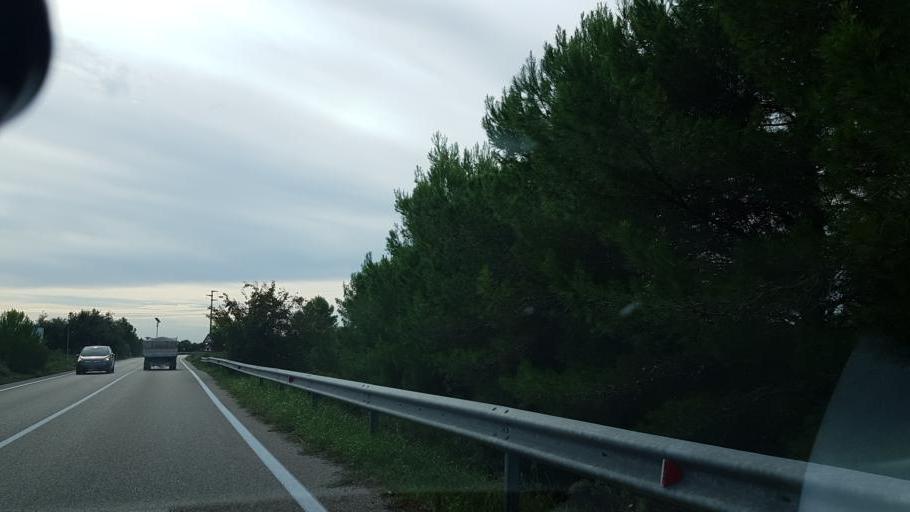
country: IT
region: Apulia
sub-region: Provincia di Lecce
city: Struda
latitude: 40.3512
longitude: 18.3207
